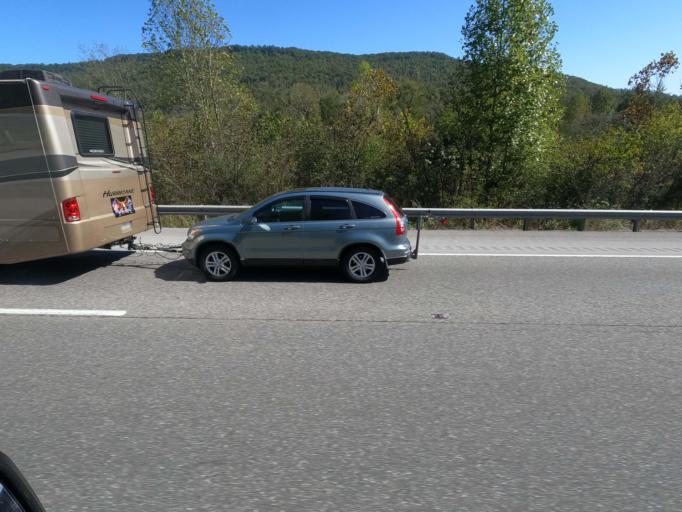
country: US
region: Tennessee
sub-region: Marion County
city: Monteagle
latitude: 35.1751
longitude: -85.7967
